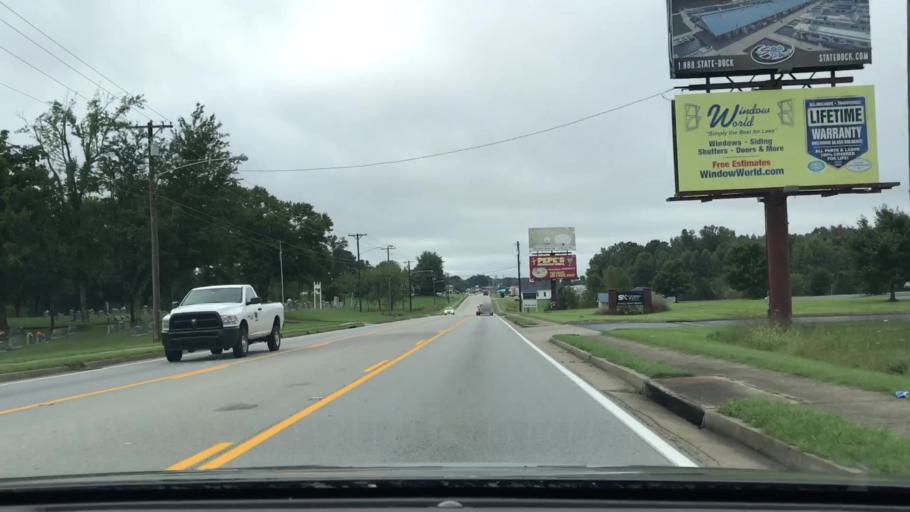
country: US
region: Kentucky
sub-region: Russell County
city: Jamestown
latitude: 37.0182
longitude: -85.0761
